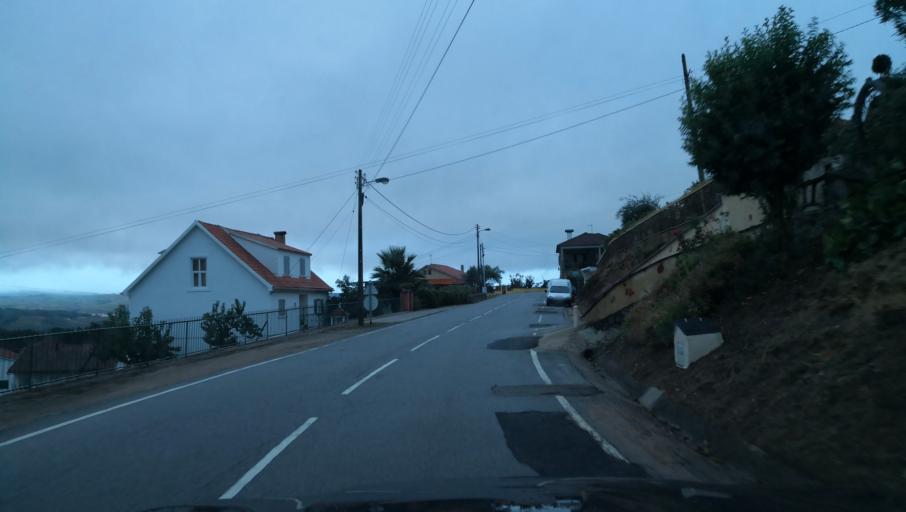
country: PT
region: Vila Real
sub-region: Sabrosa
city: Sabrosa
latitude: 41.2938
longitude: -7.5789
